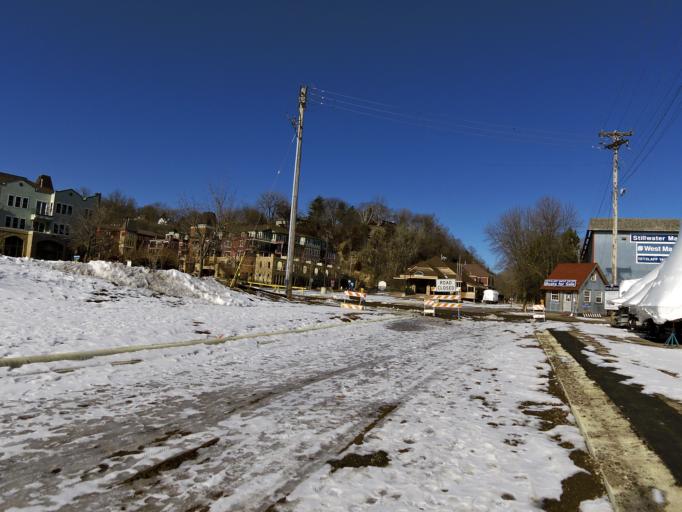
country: US
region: Minnesota
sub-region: Washington County
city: Stillwater
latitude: 45.0614
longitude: -92.8061
